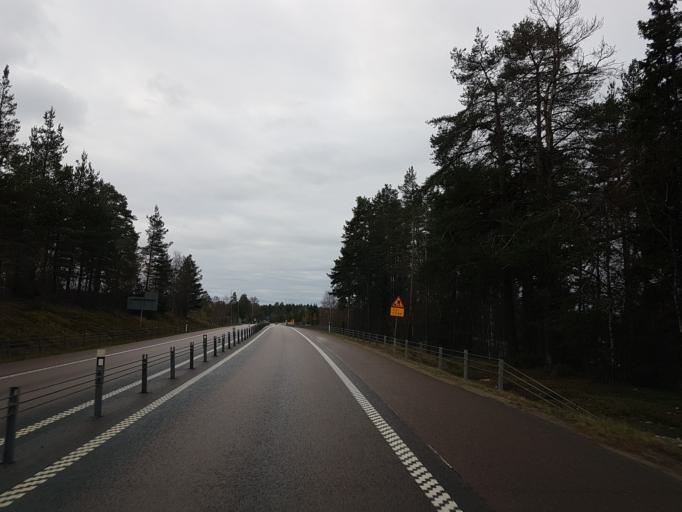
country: SE
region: Gaevleborg
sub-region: Hudiksvalls Kommun
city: Hudiksvall
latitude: 61.8011
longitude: 17.1726
